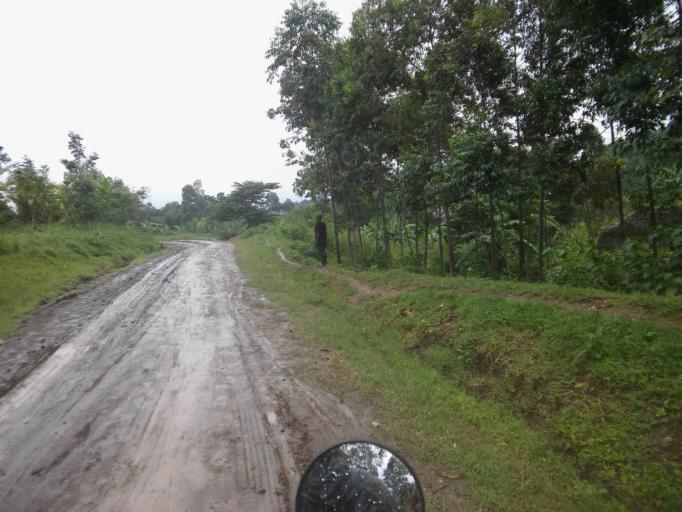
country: UG
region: Eastern Region
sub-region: Mbale District
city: Mbale
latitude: 1.0130
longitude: 34.2299
